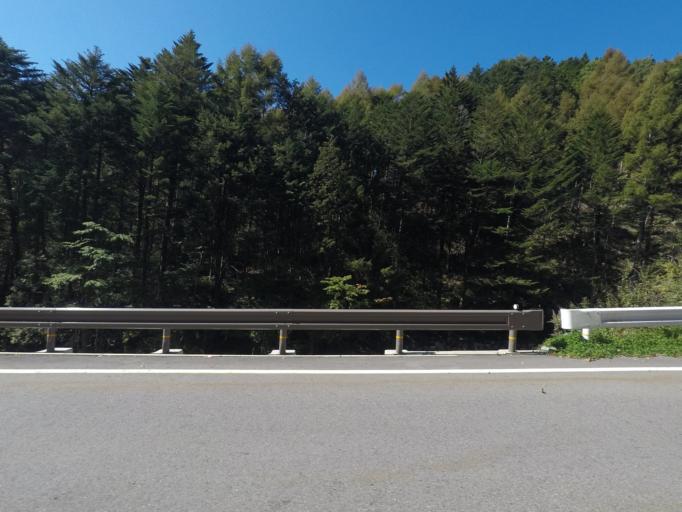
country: JP
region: Nagano
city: Shiojiri
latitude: 36.0054
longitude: 137.7350
